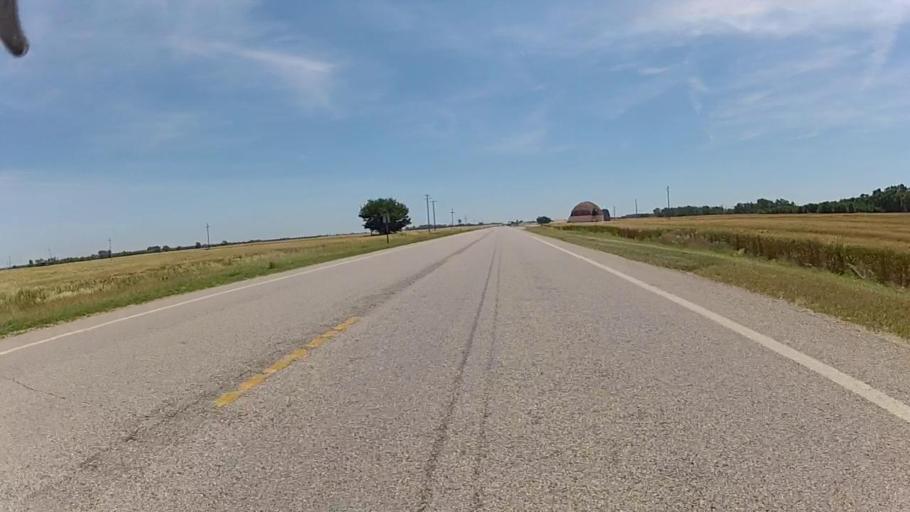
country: US
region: Kansas
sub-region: Barber County
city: Medicine Lodge
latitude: 37.2543
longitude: -98.5152
